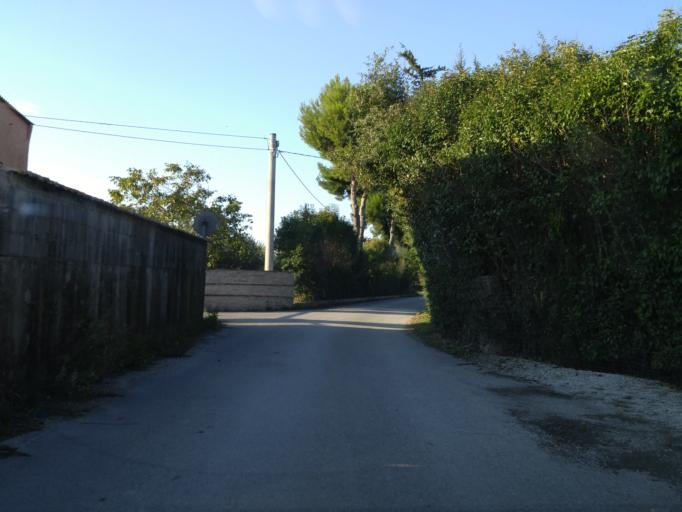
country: IT
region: The Marches
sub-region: Provincia di Pesaro e Urbino
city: Fano
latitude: 43.8143
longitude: 13.0321
